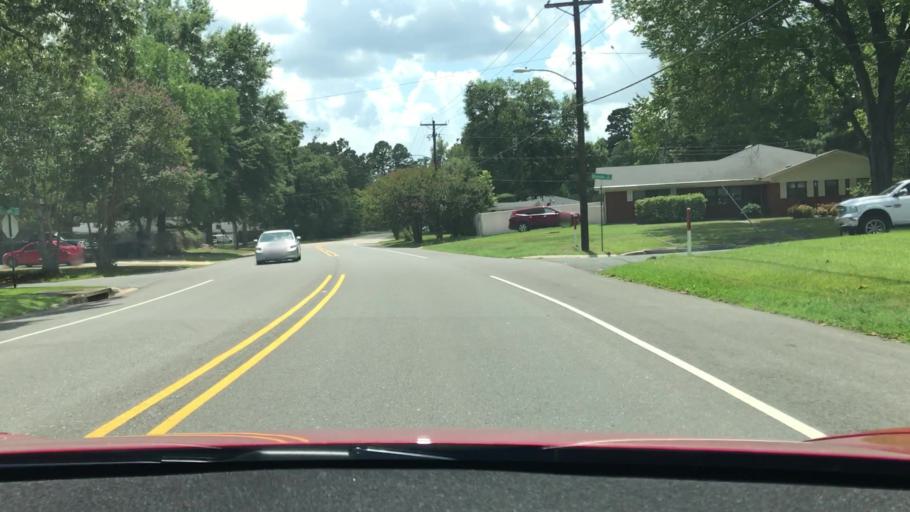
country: US
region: Louisiana
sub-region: De Soto Parish
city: Stonewall
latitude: 32.3903
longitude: -93.7849
